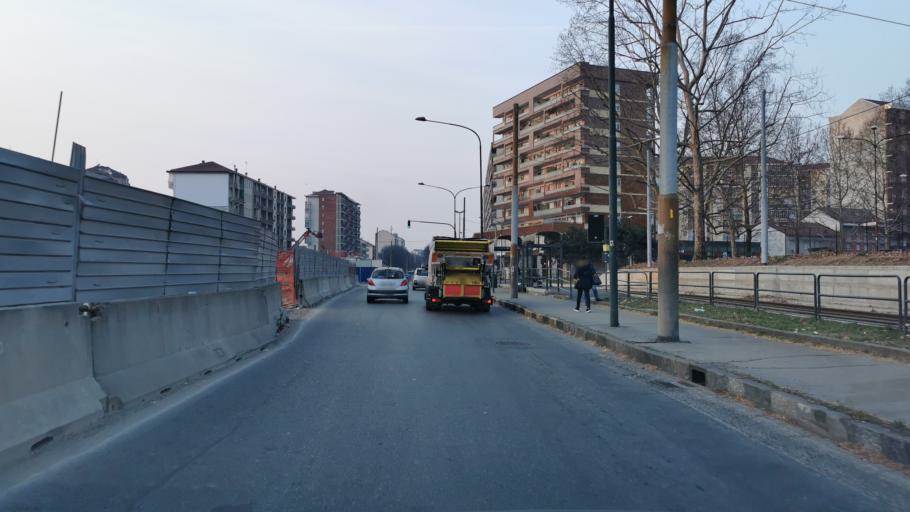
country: IT
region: Piedmont
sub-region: Provincia di Torino
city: Venaria Reale
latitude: 45.1043
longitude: 7.6626
